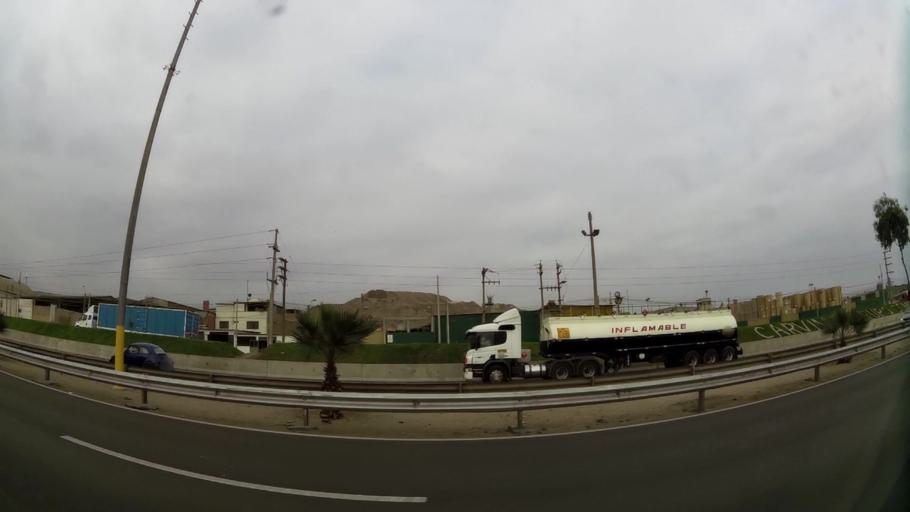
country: PE
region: Lima
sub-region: Lima
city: Surco
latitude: -12.2150
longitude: -76.9766
